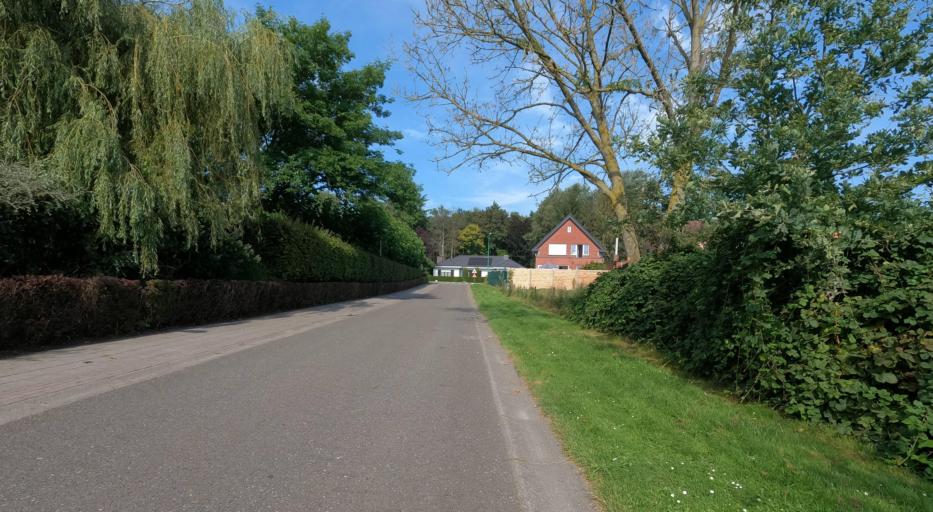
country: BE
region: Flanders
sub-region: Provincie Antwerpen
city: Essen
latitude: 51.4640
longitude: 4.4678
